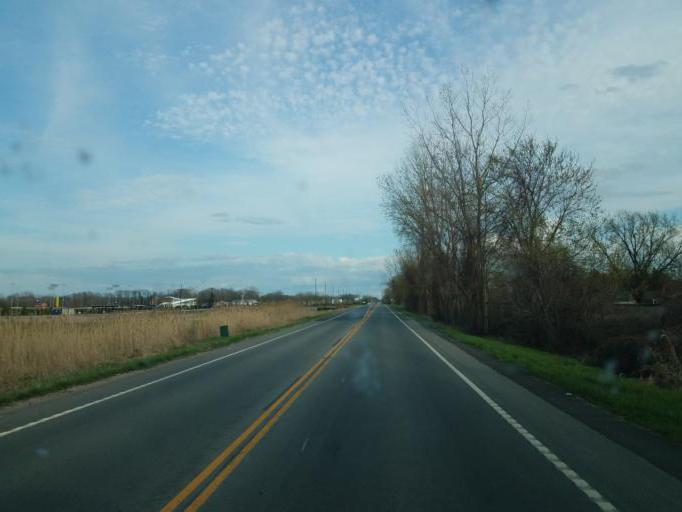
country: US
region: Ohio
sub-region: Erie County
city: Sandusky
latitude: 41.4314
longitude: -82.6572
